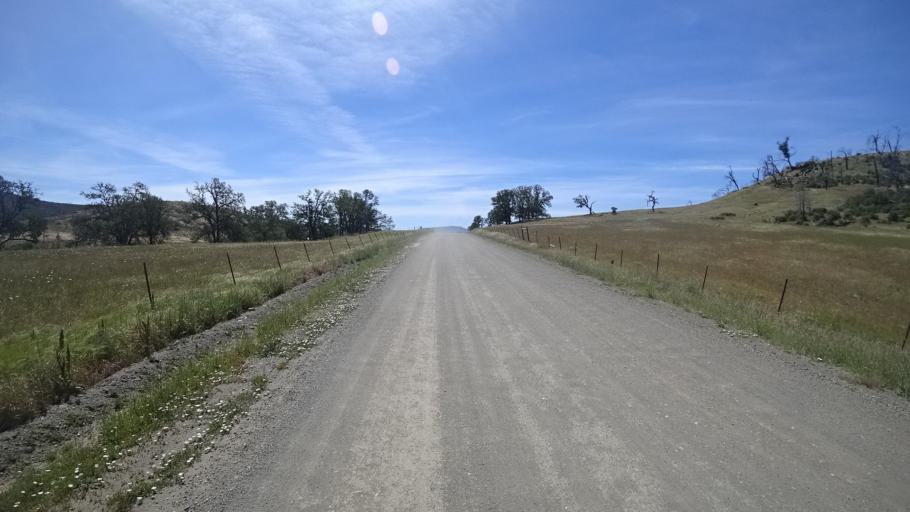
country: US
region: California
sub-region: Lake County
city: Middletown
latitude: 38.7899
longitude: -122.6122
